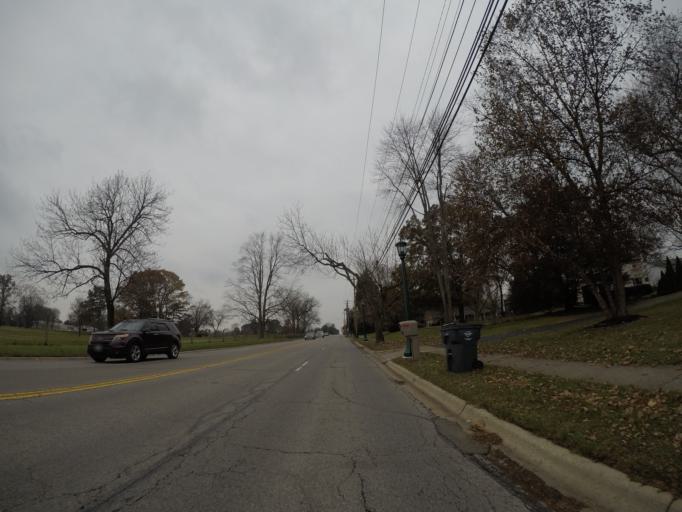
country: US
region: Ohio
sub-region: Franklin County
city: Upper Arlington
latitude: 40.0402
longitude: -83.0543
